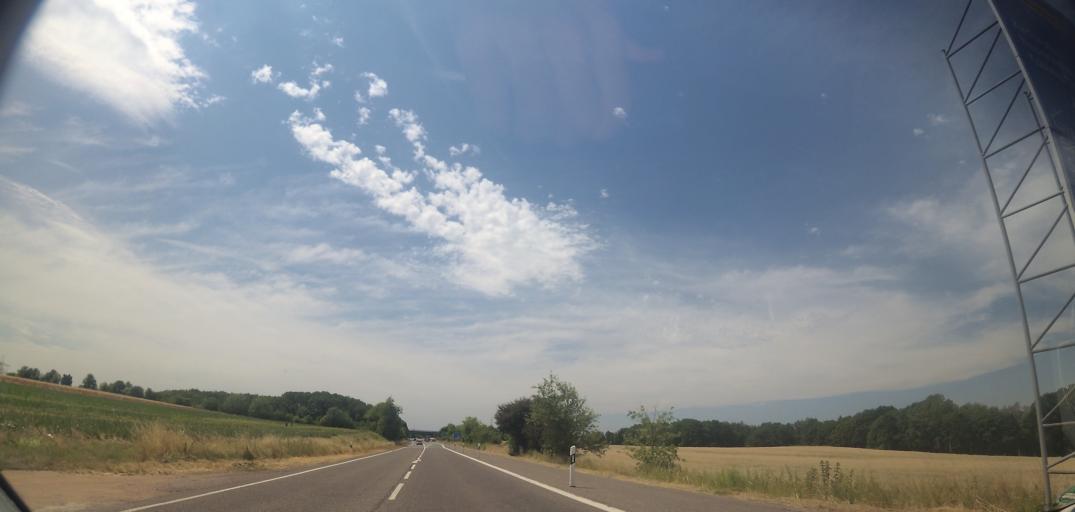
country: DE
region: Saarland
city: Saarwellingen
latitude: 49.3461
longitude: 6.7973
